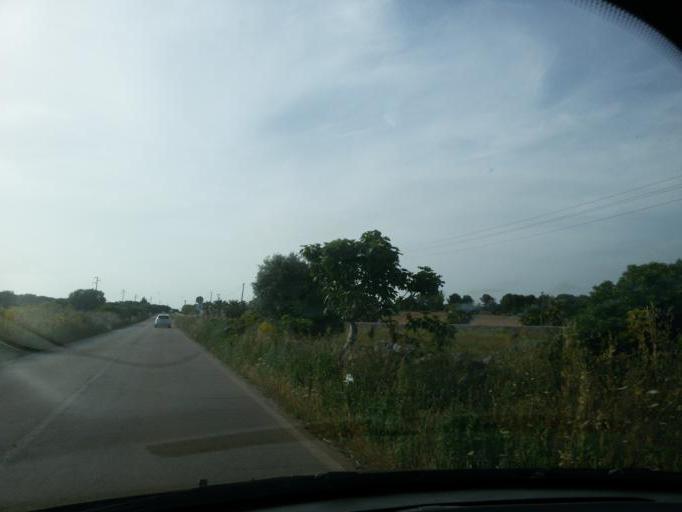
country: IT
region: Apulia
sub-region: Provincia di Lecce
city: Porto Cesareo
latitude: 40.3227
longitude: 17.8561
